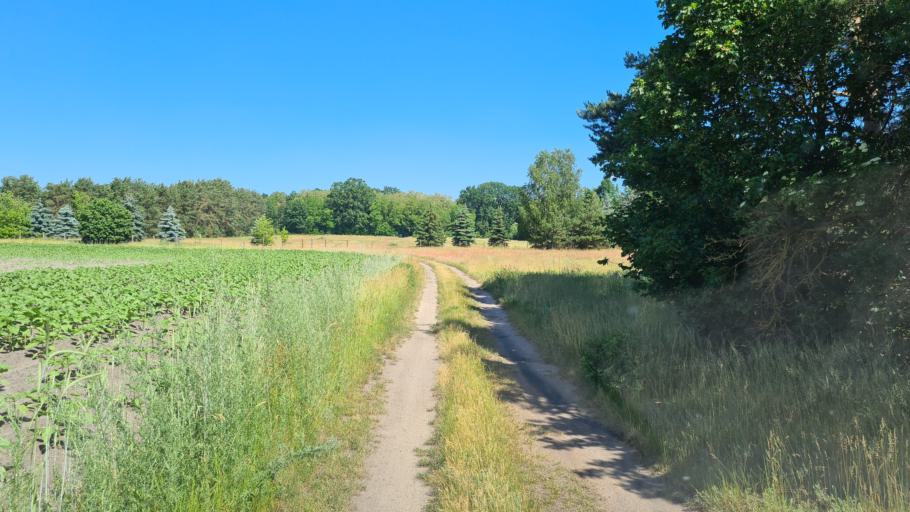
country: DE
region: Brandenburg
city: Plessa
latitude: 51.4694
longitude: 13.6436
